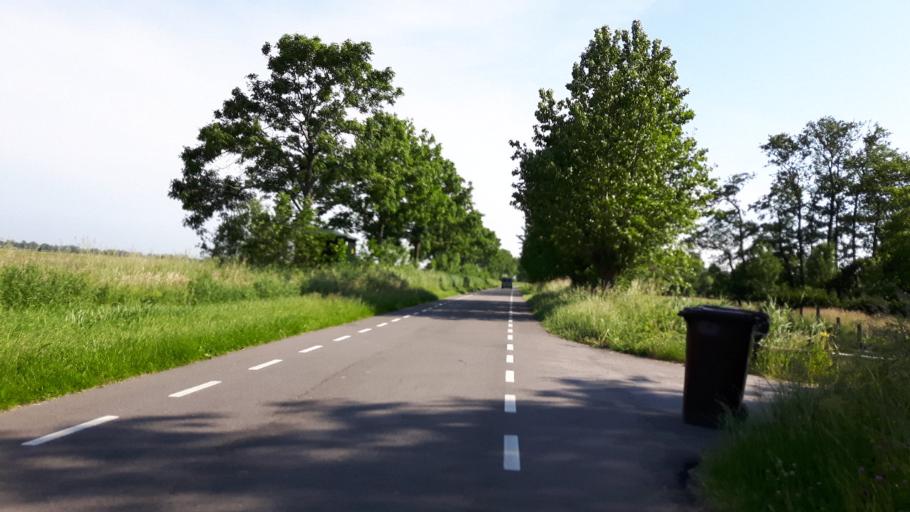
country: NL
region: Utrecht
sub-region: Stichtse Vecht
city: Breukelen
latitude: 52.1910
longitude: 4.9592
